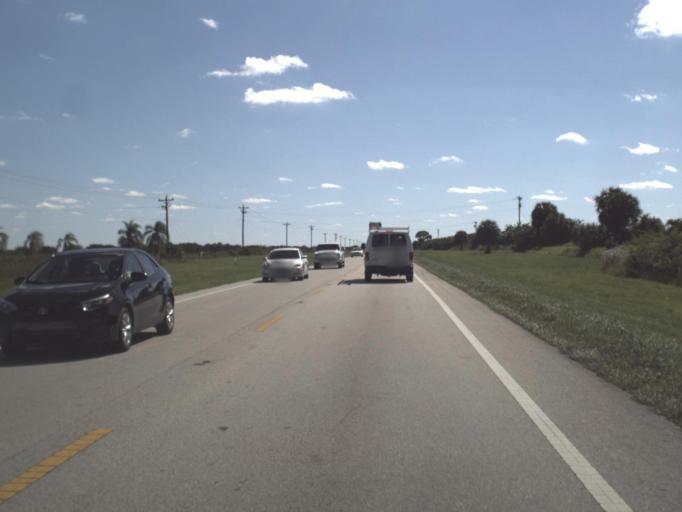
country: US
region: Florida
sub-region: Collier County
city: Immokalee
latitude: 26.4934
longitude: -81.4652
